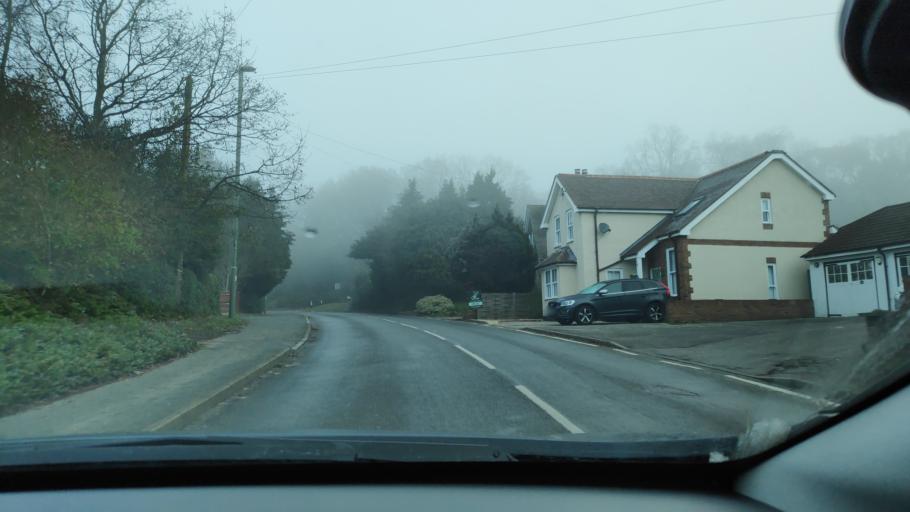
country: GB
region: England
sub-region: Surrey
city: Seale
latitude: 51.2523
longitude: -0.7109
